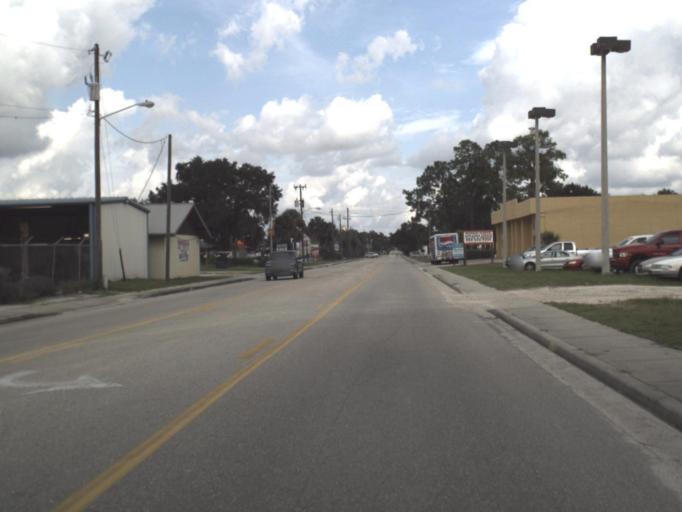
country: US
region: Florida
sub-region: Hendry County
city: LaBelle
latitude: 26.7543
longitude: -81.4373
